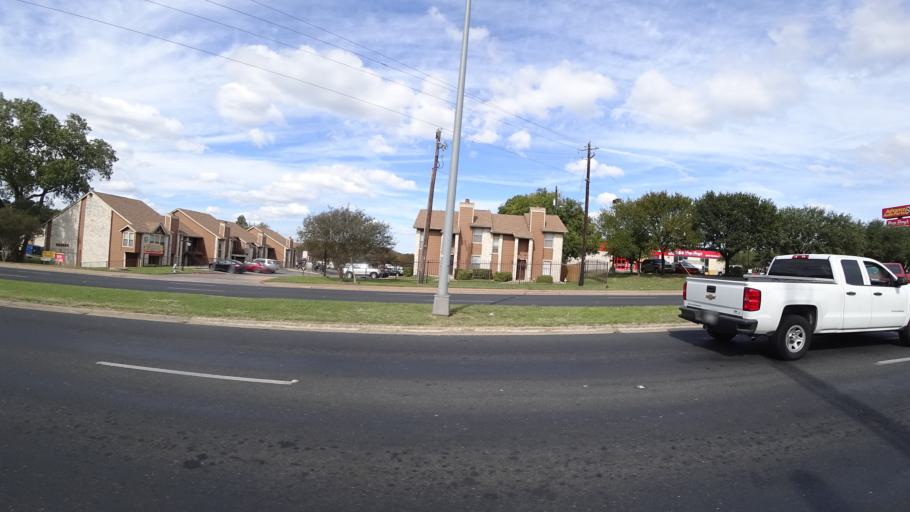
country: US
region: Texas
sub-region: Travis County
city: Onion Creek
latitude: 30.1915
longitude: -97.7737
